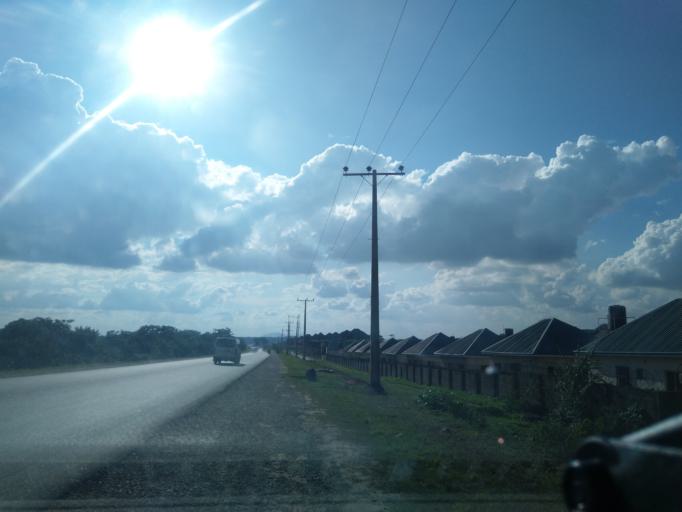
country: NG
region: Abuja Federal Capital Territory
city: Abuja
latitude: 9.0408
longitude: 7.3969
